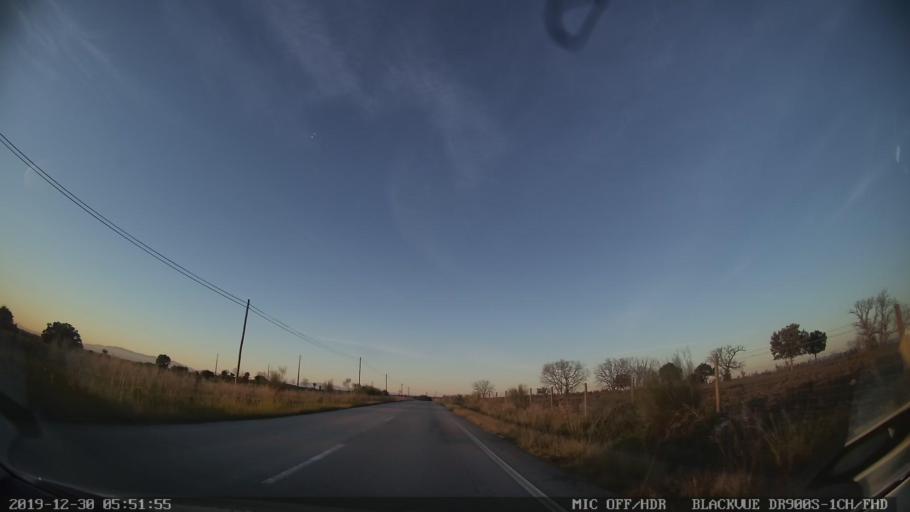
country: PT
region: Castelo Branco
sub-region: Idanha-A-Nova
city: Idanha-a-Nova
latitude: 39.9999
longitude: -7.2468
